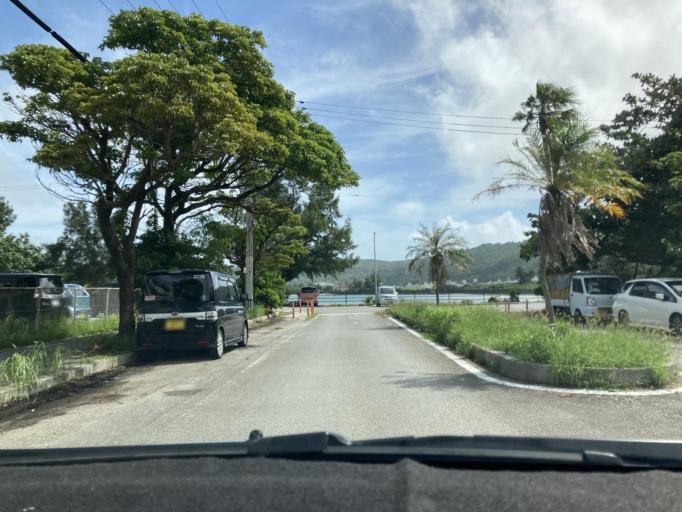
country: JP
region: Okinawa
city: Ginowan
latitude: 26.1745
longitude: 127.7782
